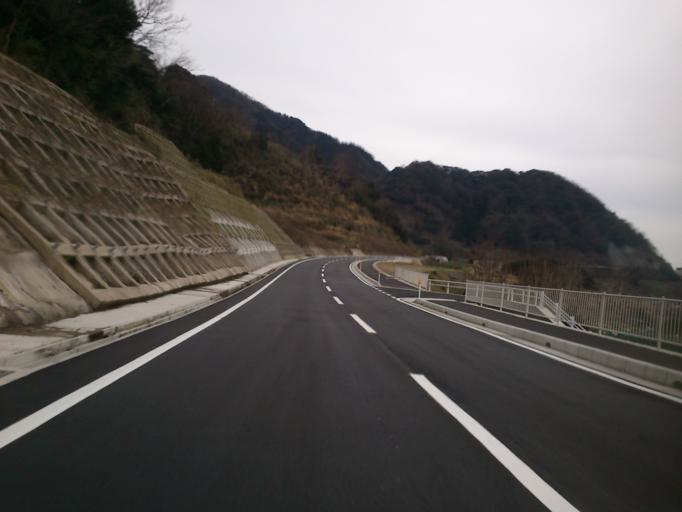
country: JP
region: Kyoto
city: Miyazu
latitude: 35.7463
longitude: 135.2544
